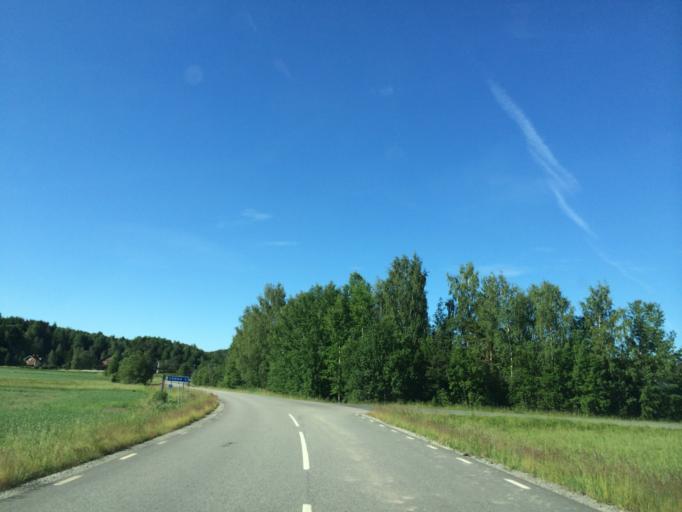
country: SE
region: OErebro
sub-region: Askersunds Kommun
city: Askersund
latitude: 58.7868
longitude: 15.0021
